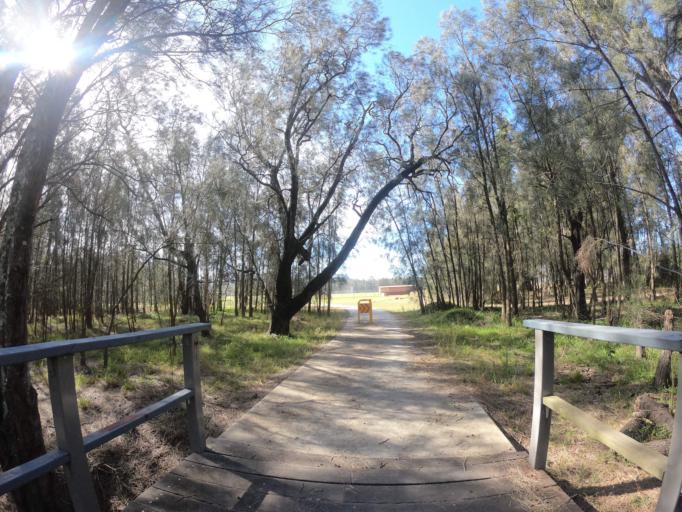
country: AU
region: New South Wales
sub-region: Wollongong
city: Berkeley
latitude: -34.4851
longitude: 150.8369
